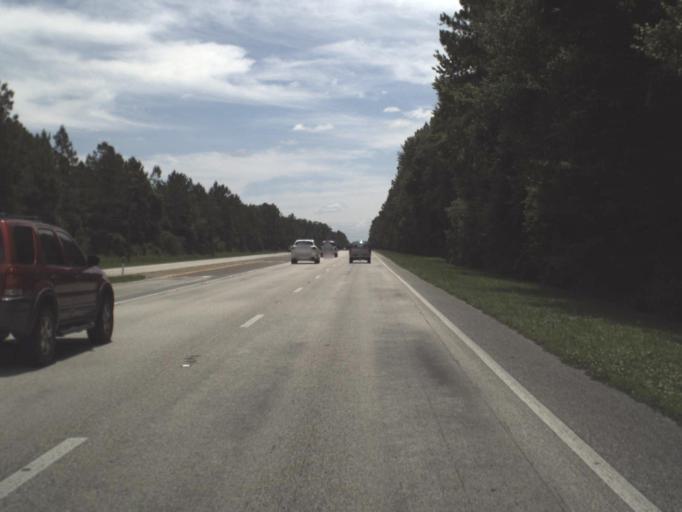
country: US
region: Florida
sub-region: Nassau County
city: Nassau Village-Ratliff
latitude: 30.4655
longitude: -81.7766
